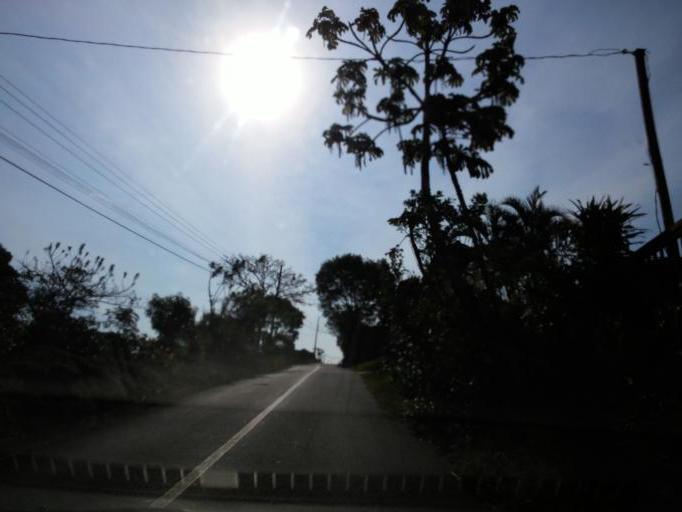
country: CR
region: Heredia
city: Santo Domingo
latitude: 10.0787
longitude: -84.1830
